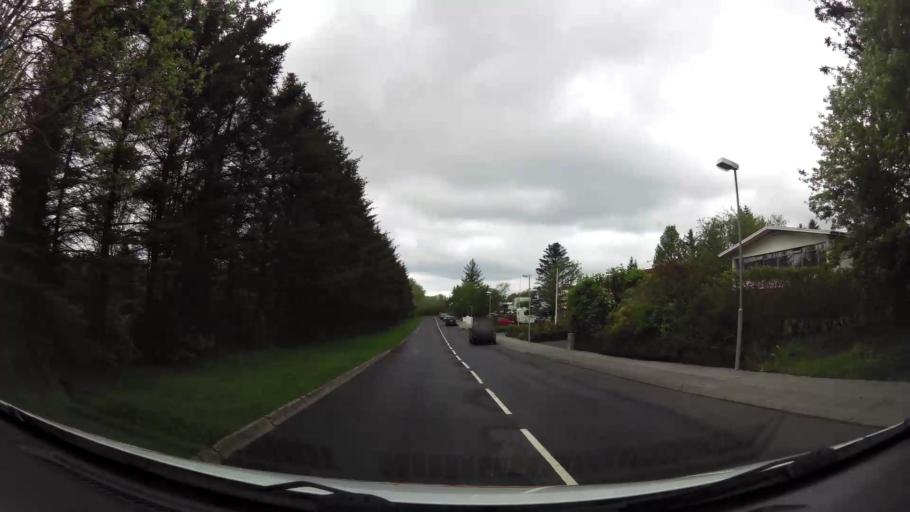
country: IS
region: Capital Region
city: Reykjavik
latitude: 64.1400
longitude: -21.8635
